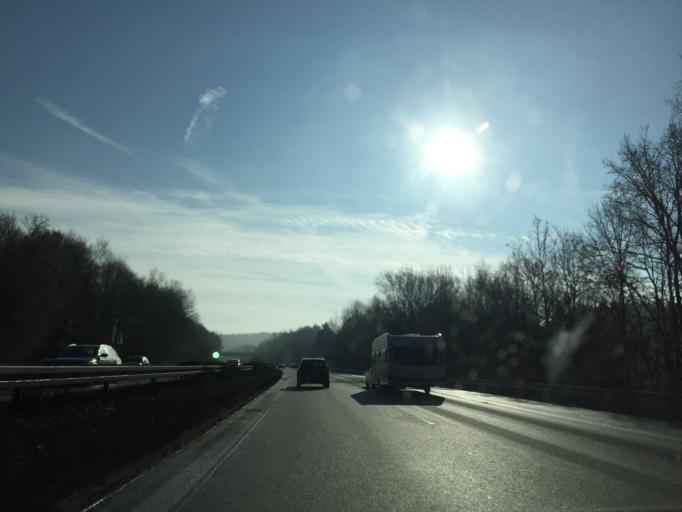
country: DE
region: Bavaria
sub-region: Regierungsbezirk Mittelfranken
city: Vestenbergsgreuth
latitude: 49.7345
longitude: 10.6622
